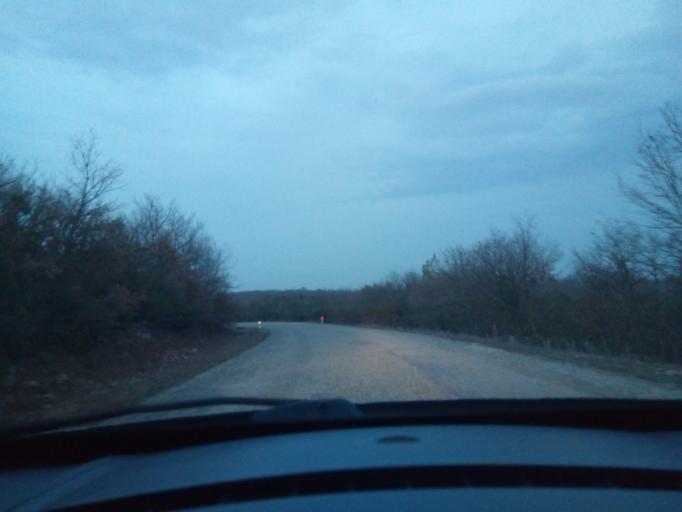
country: TR
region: Balikesir
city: Omerkoy
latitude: 39.9154
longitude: 28.0562
